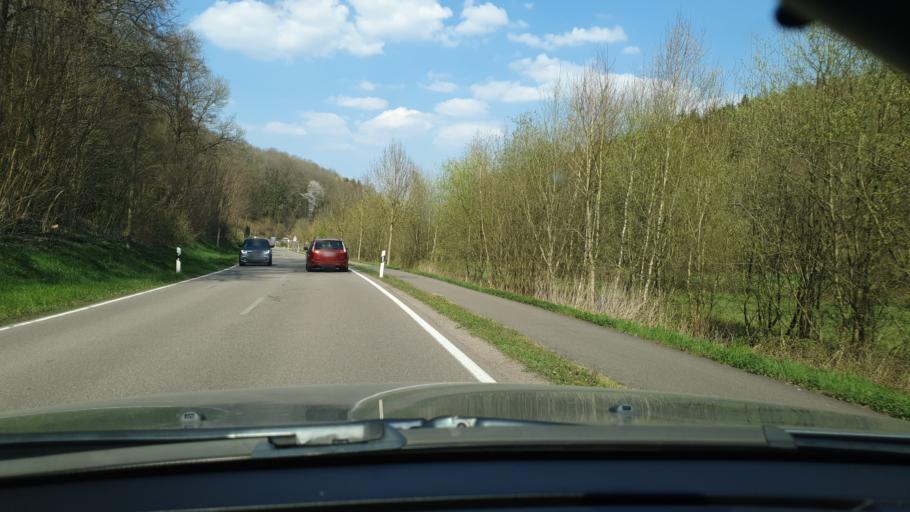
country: DE
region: Rheinland-Pfalz
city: Contwig
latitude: 49.2624
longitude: 7.4022
